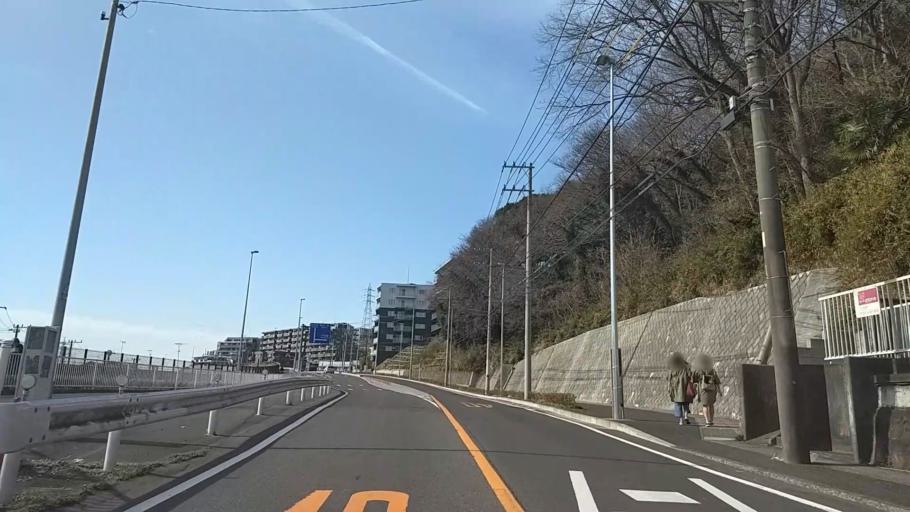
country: JP
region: Kanagawa
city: Kamakura
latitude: 35.4011
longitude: 139.5474
